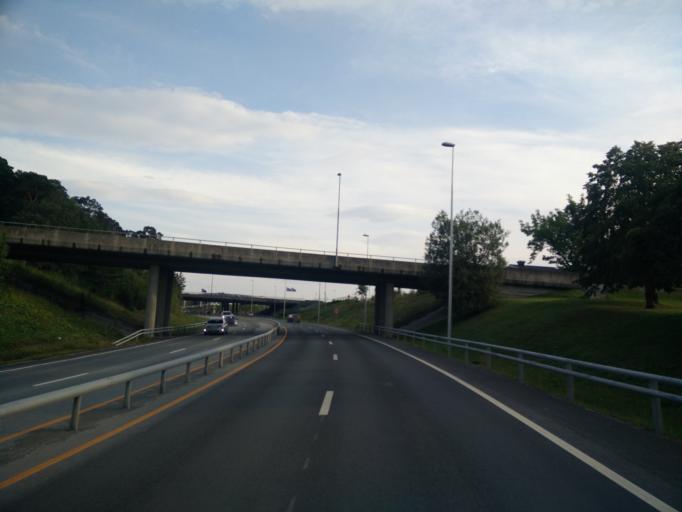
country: NO
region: Sor-Trondelag
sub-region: Trondheim
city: Trondheim
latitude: 63.4339
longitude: 10.4725
